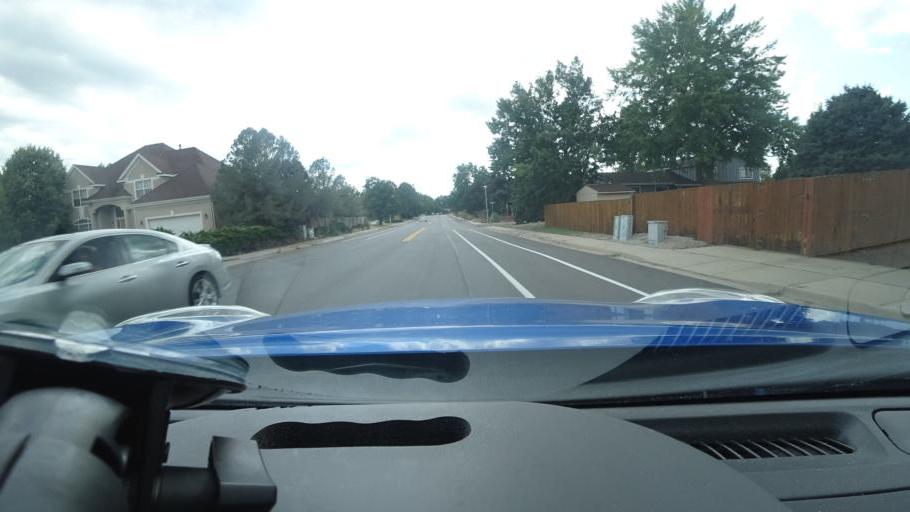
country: US
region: Colorado
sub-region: Adams County
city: Aurora
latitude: 39.6896
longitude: -104.8581
